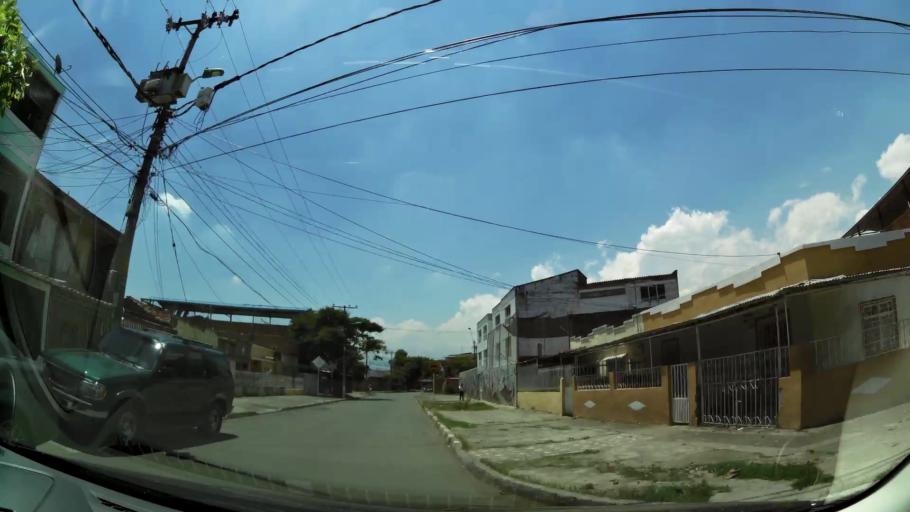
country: CO
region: Valle del Cauca
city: Cali
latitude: 3.4320
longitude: -76.5044
